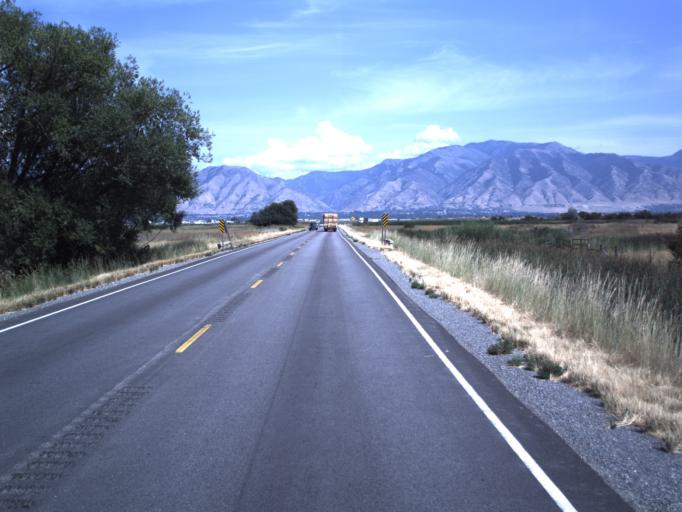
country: US
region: Utah
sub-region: Cache County
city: Benson
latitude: 41.7458
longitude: -111.9358
